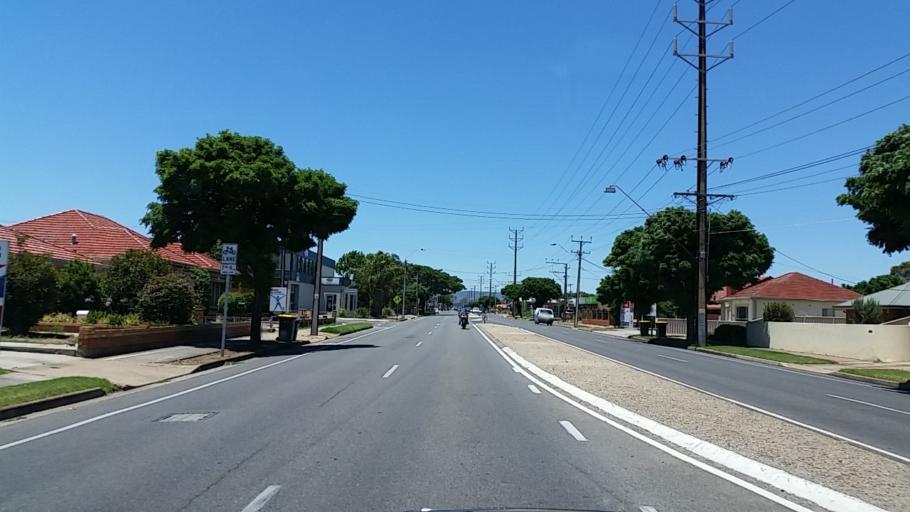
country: AU
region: South Australia
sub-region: Charles Sturt
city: Findon
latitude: -34.9053
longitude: 138.5364
